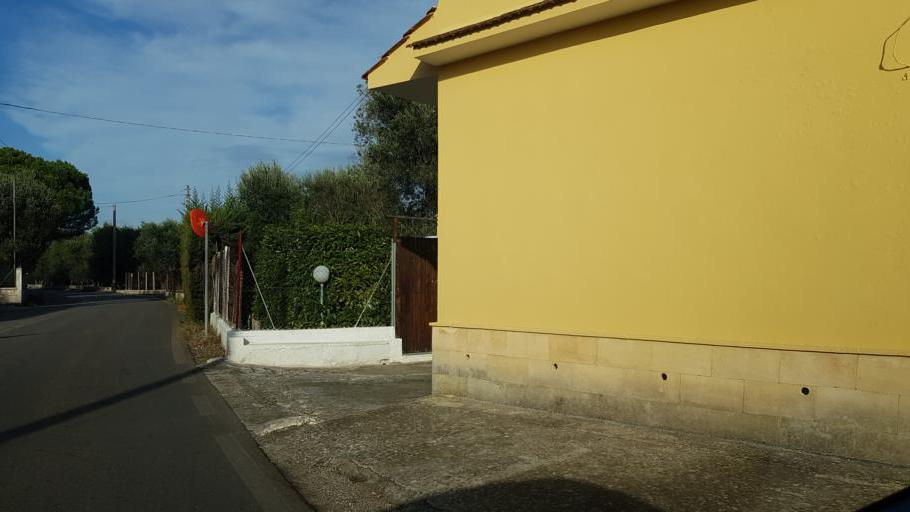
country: IT
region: Apulia
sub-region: Provincia di Brindisi
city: Oria
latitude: 40.5154
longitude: 17.6506
